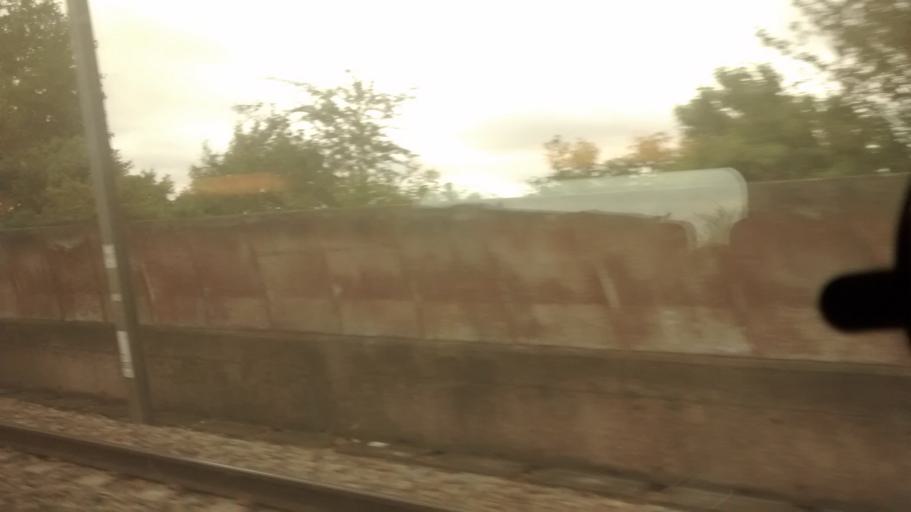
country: FR
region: Centre
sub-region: Departement d'Eure-et-Loir
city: Beville-le-Comte
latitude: 48.3882
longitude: 1.7274
